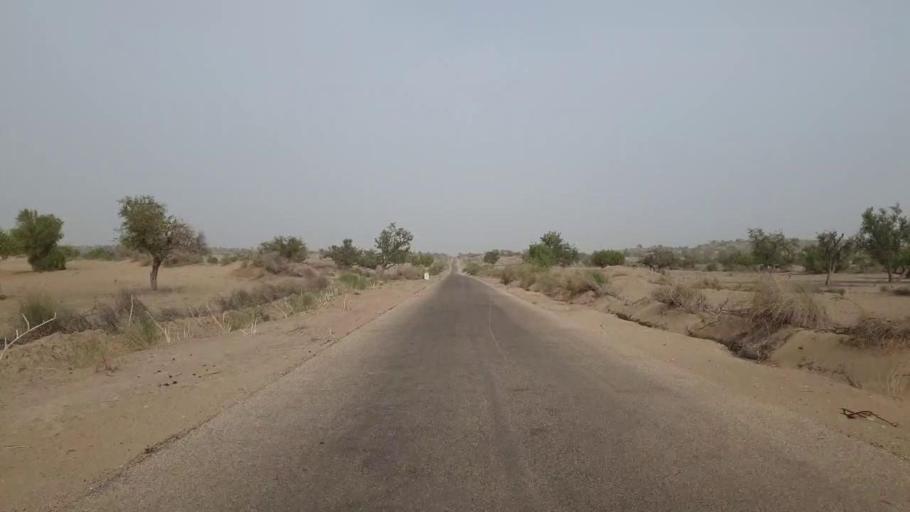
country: PK
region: Sindh
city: Islamkot
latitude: 24.5646
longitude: 70.3333
